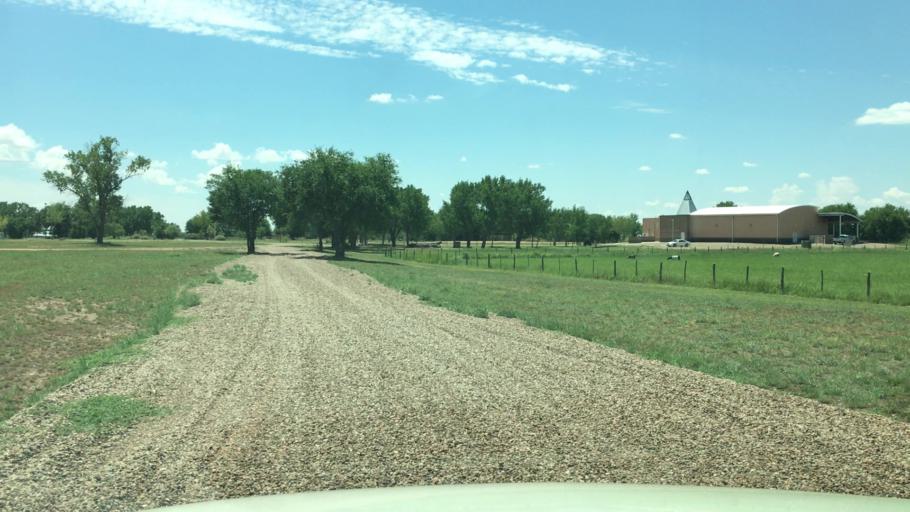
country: US
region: New Mexico
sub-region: De Baca County
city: Fort Sumner
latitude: 34.4039
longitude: -104.1944
